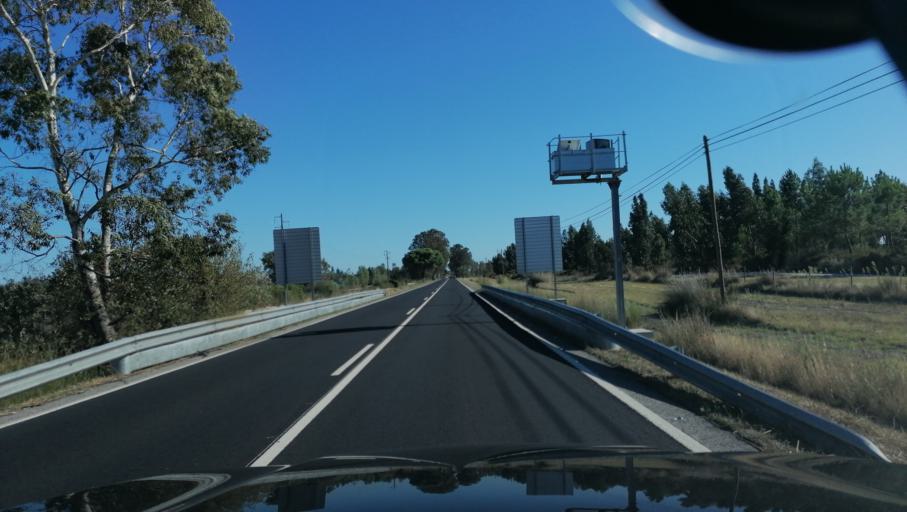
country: PT
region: Setubal
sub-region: Alcochete
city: Alcochete
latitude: 38.7934
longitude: -8.8808
